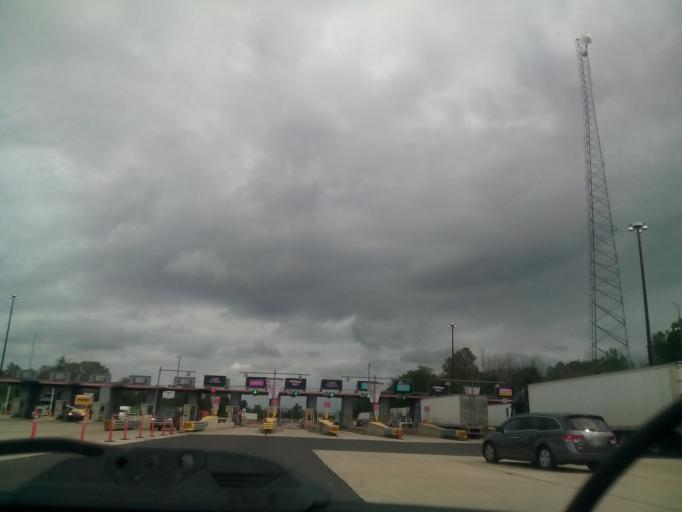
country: US
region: Indiana
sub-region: Steuben County
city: Fremont
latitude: 41.6665
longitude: -84.8542
